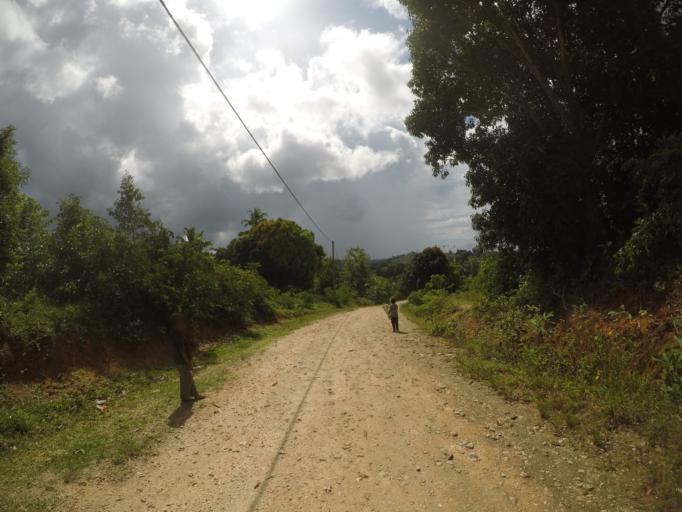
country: TZ
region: Pemba South
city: Mtambile
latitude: -5.3498
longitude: 39.6993
